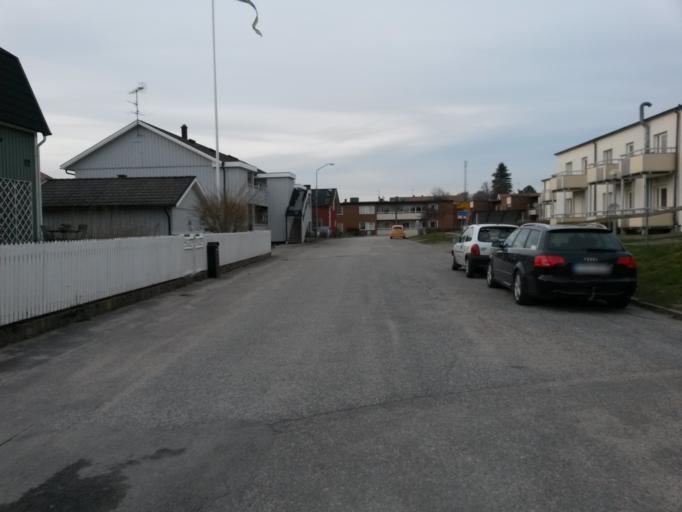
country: SE
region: Vaestra Goetaland
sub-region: Herrljunga Kommun
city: Herrljunga
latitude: 58.0766
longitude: 13.0290
